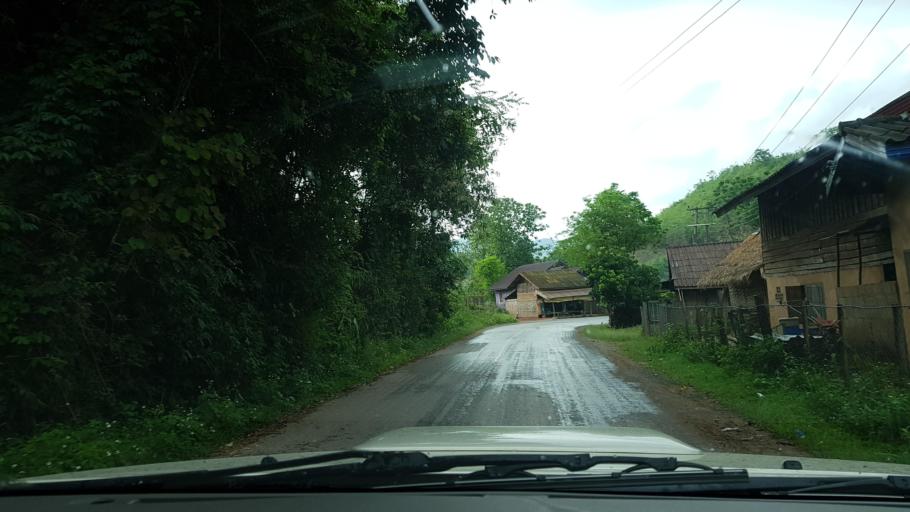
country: LA
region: Oudomxai
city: Muang Xay
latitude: 20.5809
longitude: 101.9203
